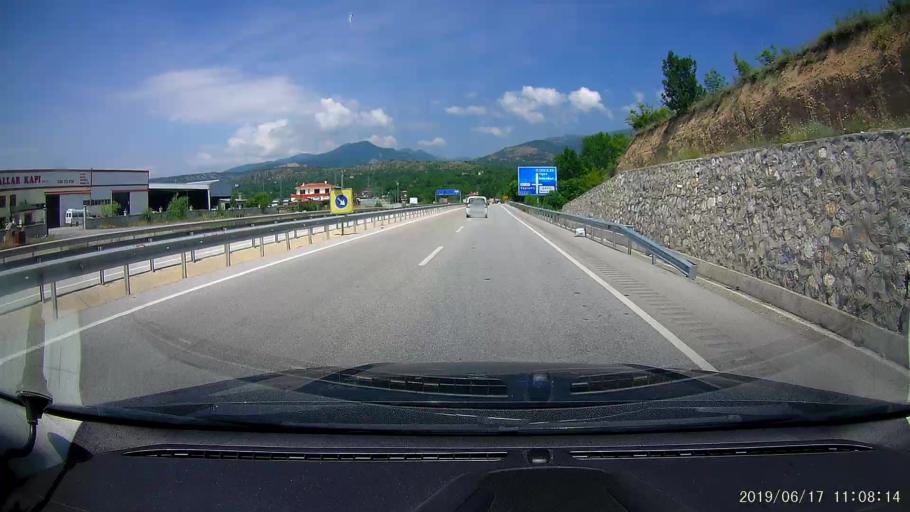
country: TR
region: Kastamonu
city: Tosya
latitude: 41.0004
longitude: 34.0402
